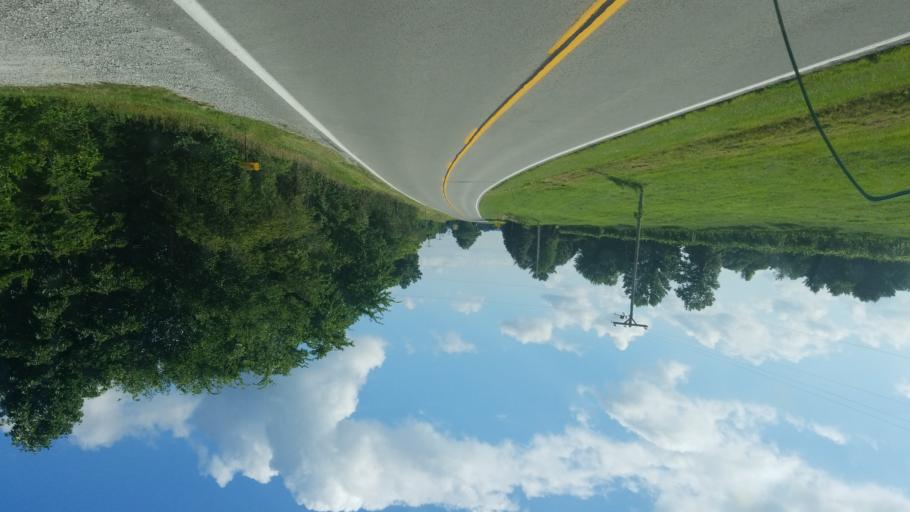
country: US
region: Illinois
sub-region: Union County
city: Cobden
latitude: 37.5805
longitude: -89.3207
